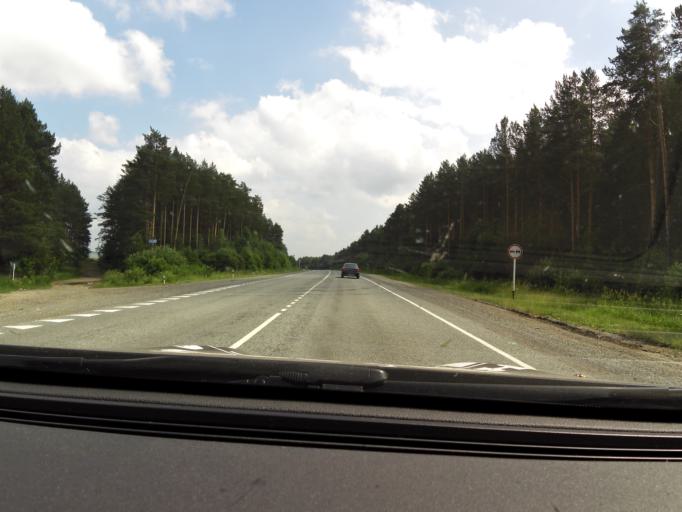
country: RU
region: Sverdlovsk
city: Achit
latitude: 56.8006
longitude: 57.8491
